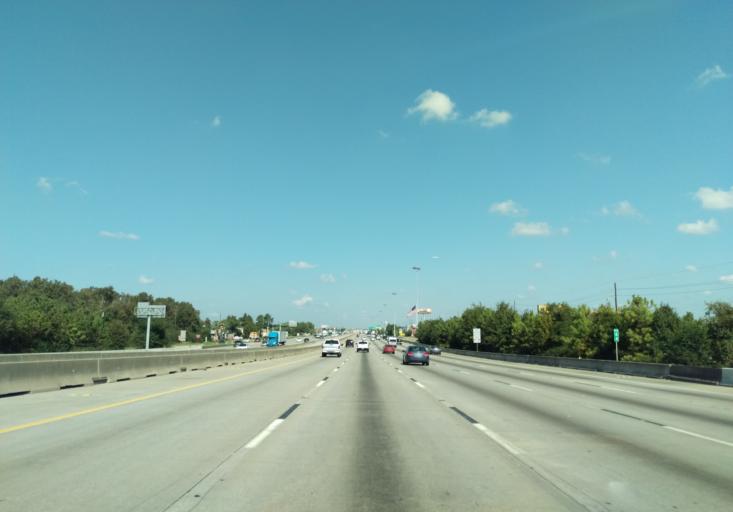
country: US
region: Texas
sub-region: Harris County
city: Aldine
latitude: 29.9840
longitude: -95.4230
